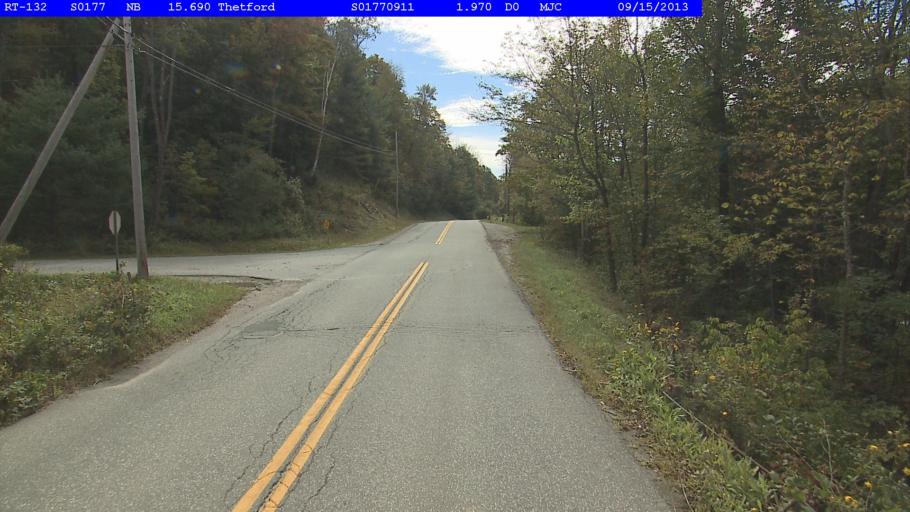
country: US
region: New Hampshire
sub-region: Grafton County
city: Hanover
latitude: 43.8268
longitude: -72.2866
